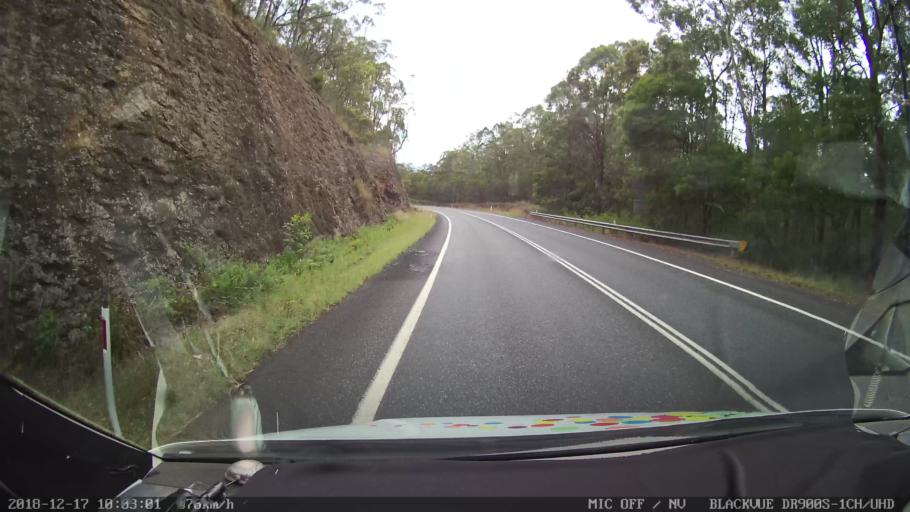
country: AU
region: New South Wales
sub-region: Tenterfield Municipality
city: Carrolls Creek
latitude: -28.8996
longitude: 152.4584
